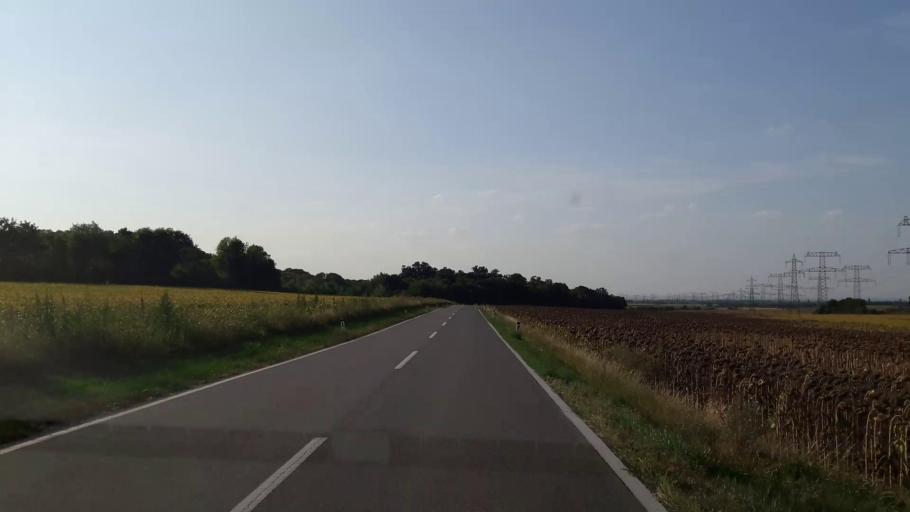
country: AT
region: Lower Austria
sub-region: Politischer Bezirk Ganserndorf
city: Orth an der Donau
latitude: 48.0844
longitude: 16.6746
